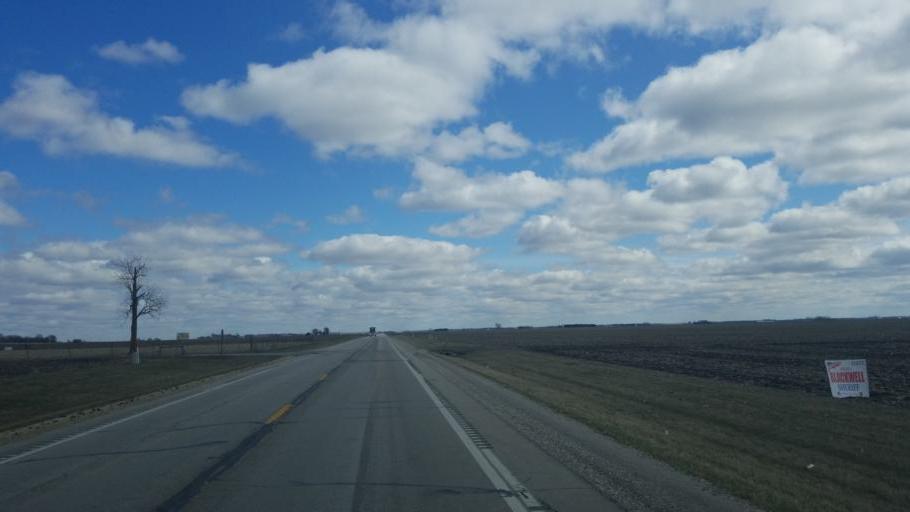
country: US
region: Illinois
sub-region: Douglas County
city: Villa Grove
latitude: 39.7918
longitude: -88.1466
